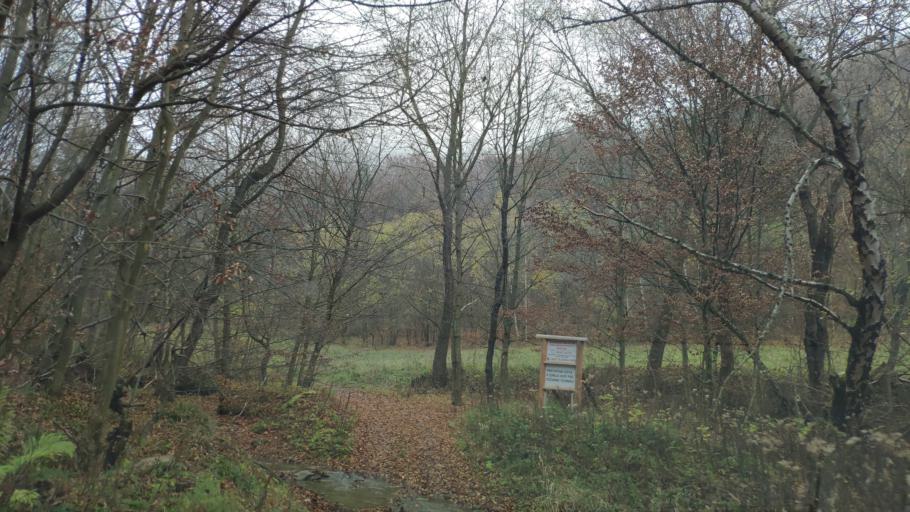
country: SK
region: Presovsky
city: Sabinov
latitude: 49.1463
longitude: 21.2136
